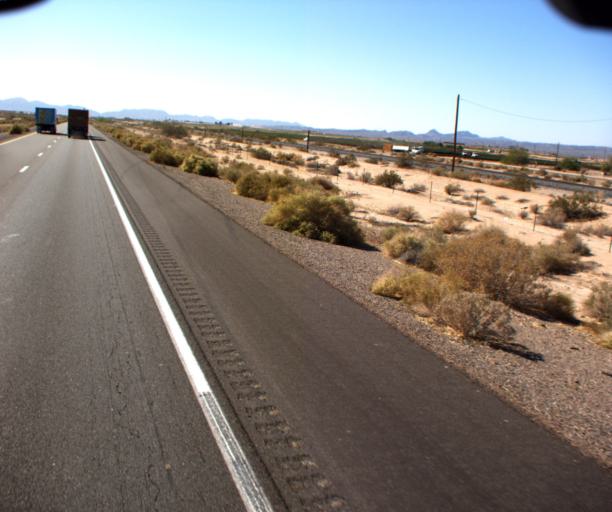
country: US
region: Arizona
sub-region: Yuma County
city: Wellton
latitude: 32.6739
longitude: -114.0816
